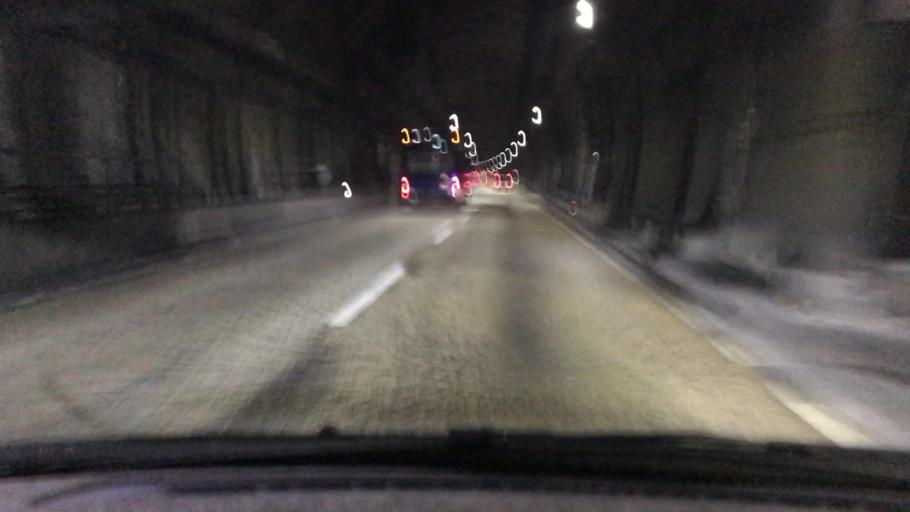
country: JP
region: Hyogo
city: Kobe
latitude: 34.7125
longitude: 135.1912
